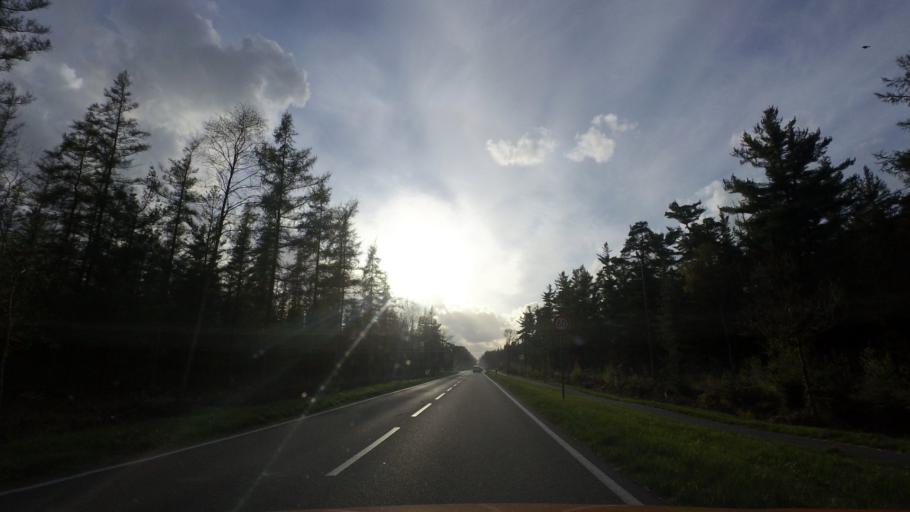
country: DE
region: Lower Saxony
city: Oldenburg
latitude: 53.1227
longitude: 8.1154
